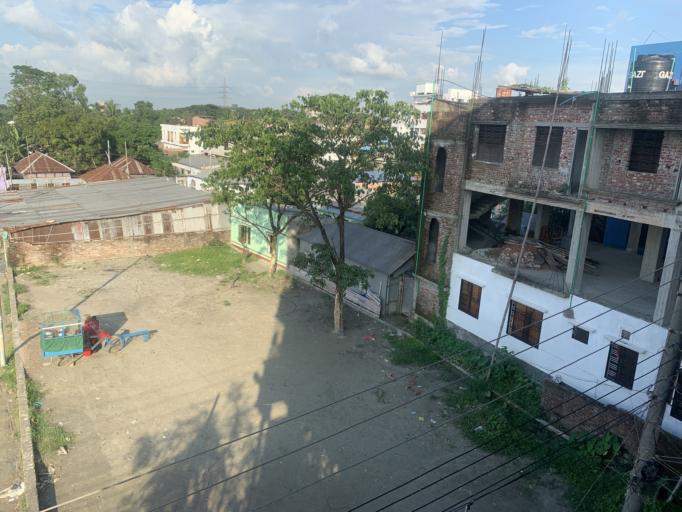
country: BD
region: Dhaka
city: Paltan
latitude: 23.7477
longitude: 90.4502
